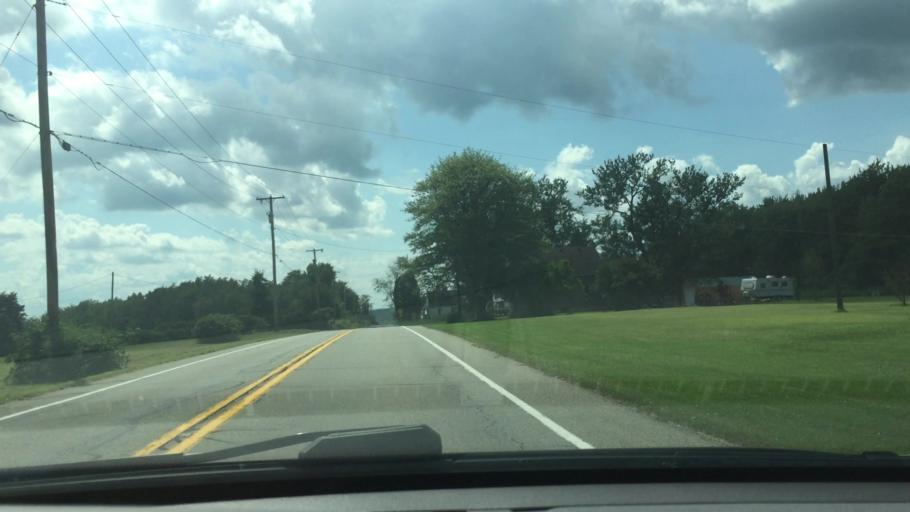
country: US
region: Pennsylvania
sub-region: Lawrence County
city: New Wilmington
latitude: 41.1196
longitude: -80.2409
